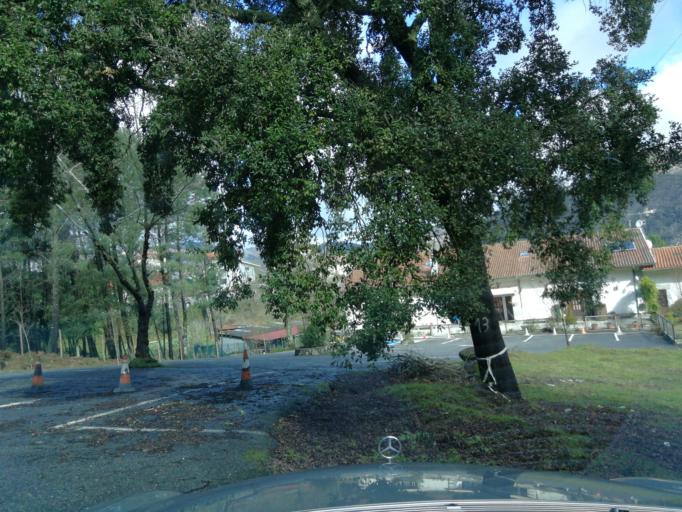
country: ES
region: Galicia
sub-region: Provincia de Ourense
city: Entrimo
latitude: 41.8708
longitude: -8.1908
